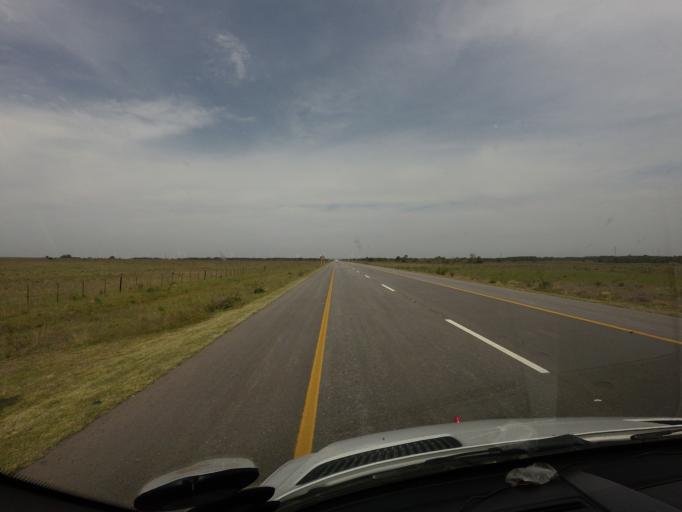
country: ZA
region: Eastern Cape
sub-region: Cacadu District Municipality
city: Kruisfontein
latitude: -34.0033
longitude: 24.7677
